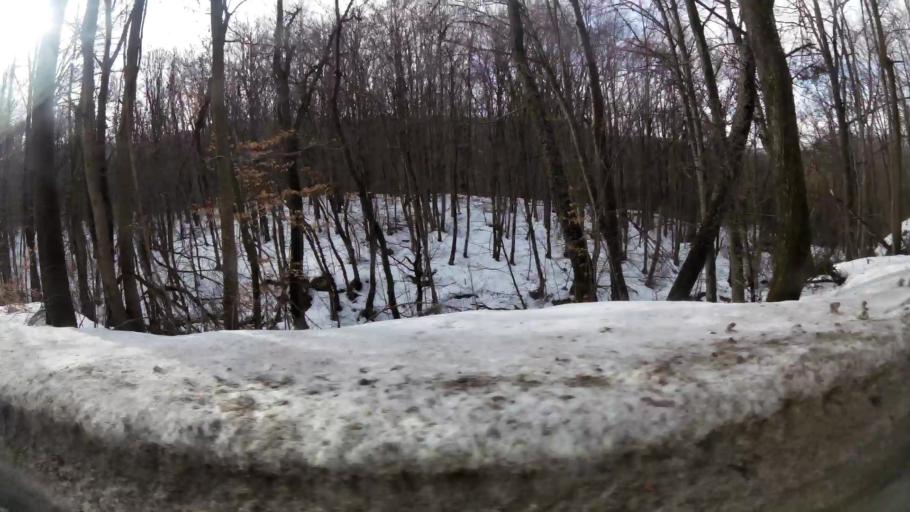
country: BG
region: Sofia-Capital
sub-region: Stolichna Obshtina
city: Sofia
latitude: 42.6331
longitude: 23.2241
